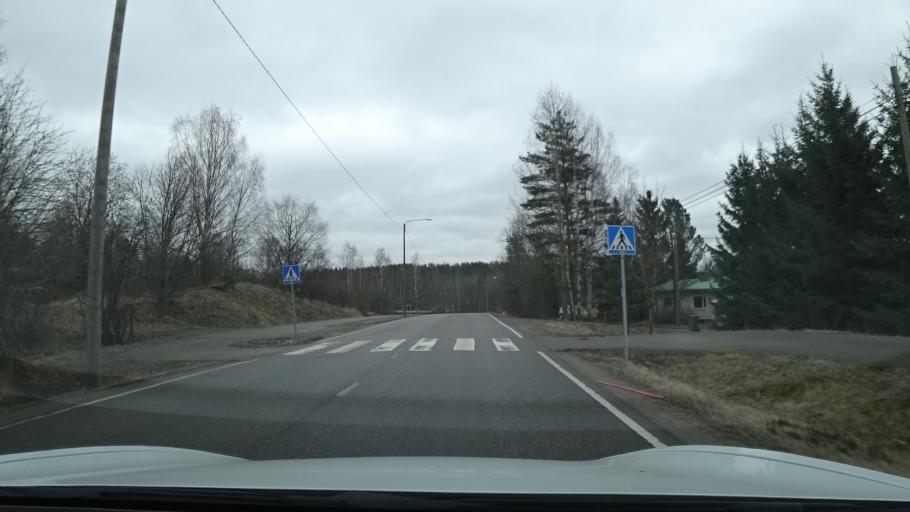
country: FI
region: Uusimaa
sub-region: Porvoo
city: Askola
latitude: 60.4965
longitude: 25.5197
